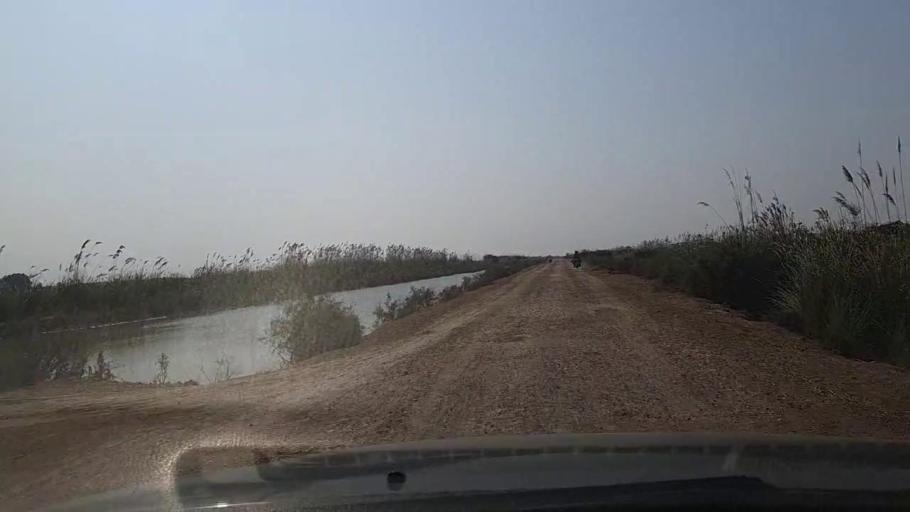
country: PK
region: Sindh
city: Mirpur Sakro
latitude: 24.3792
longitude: 67.6591
